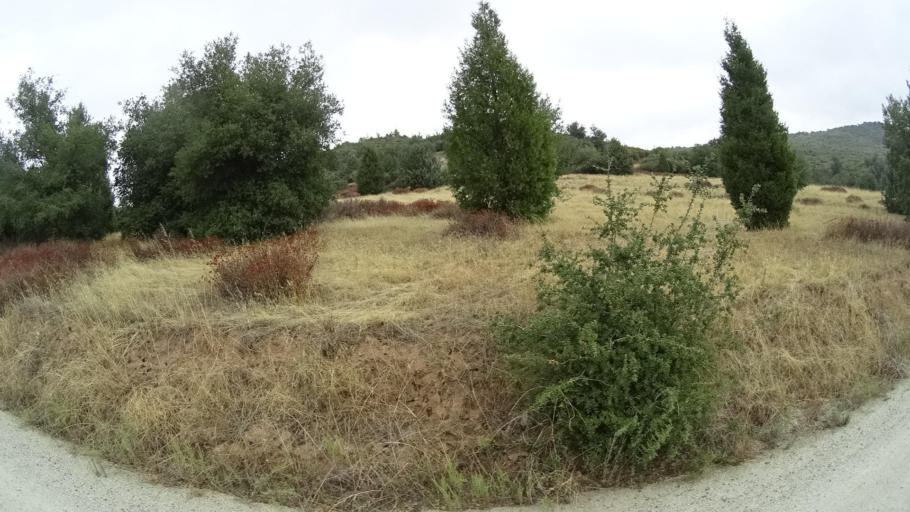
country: US
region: California
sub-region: San Diego County
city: Julian
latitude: 33.0165
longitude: -116.6345
